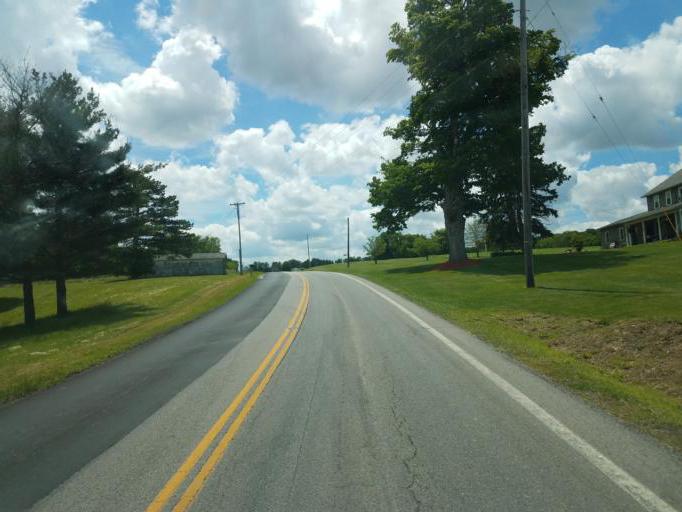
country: US
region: Ohio
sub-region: Richland County
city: Lexington
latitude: 40.6143
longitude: -82.5900
